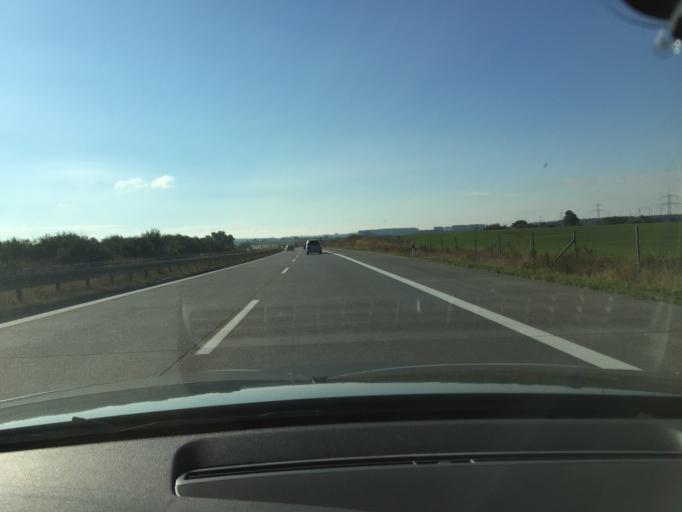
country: DE
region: Mecklenburg-Vorpommern
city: Kavelstorf
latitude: 53.9622
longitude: 12.1970
